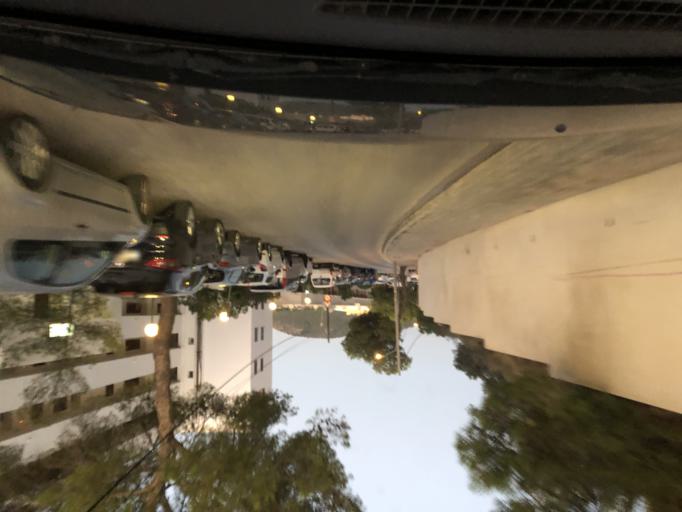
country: ES
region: Balearic Islands
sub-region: Illes Balears
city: Santa Ponsa
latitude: 39.5202
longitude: 2.4776
